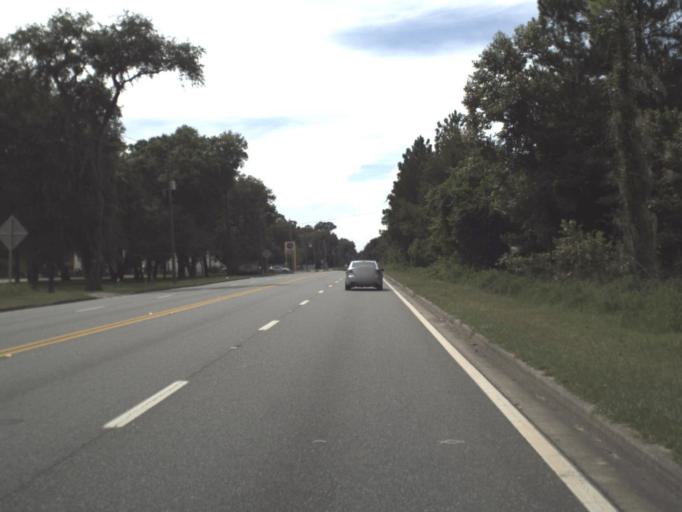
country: US
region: Florida
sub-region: Taylor County
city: Perry
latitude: 30.0897
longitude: -83.5342
